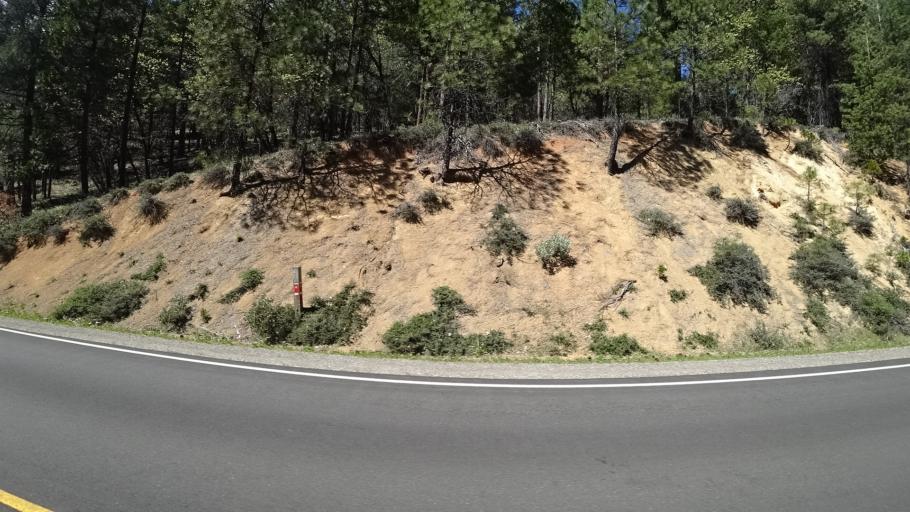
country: US
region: California
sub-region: Trinity County
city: Lewiston
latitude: 40.8801
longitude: -122.8000
